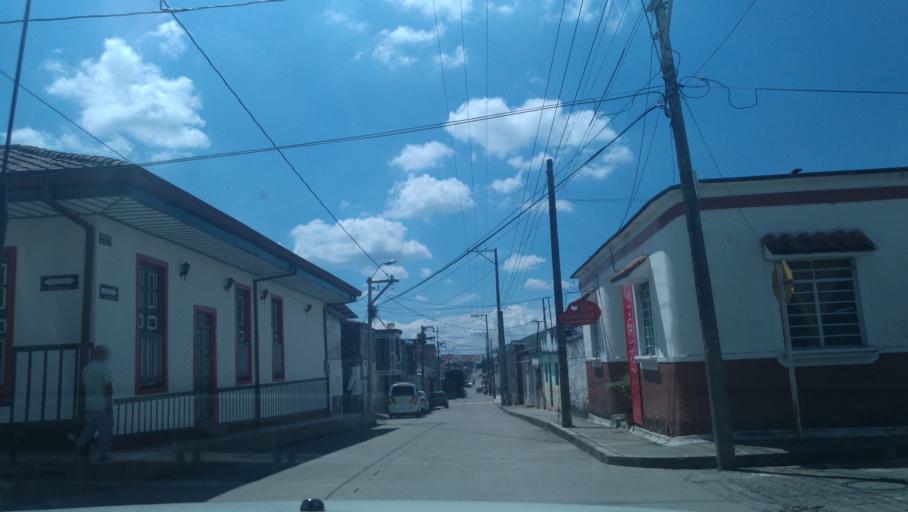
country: CO
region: Quindio
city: Circasia
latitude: 4.6212
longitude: -75.6327
